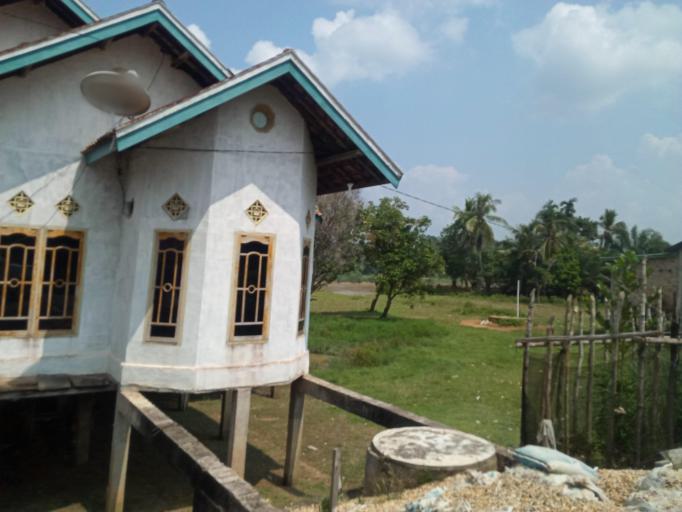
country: ID
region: Jambi
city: Mersam
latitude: -1.7064
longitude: 102.8838
